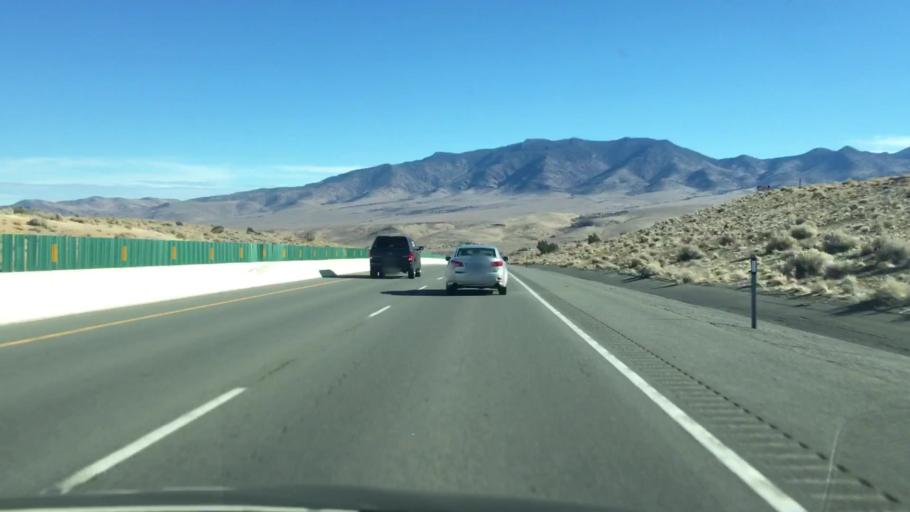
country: US
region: Nevada
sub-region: Lyon County
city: Dayton
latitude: 39.2226
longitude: -119.6228
